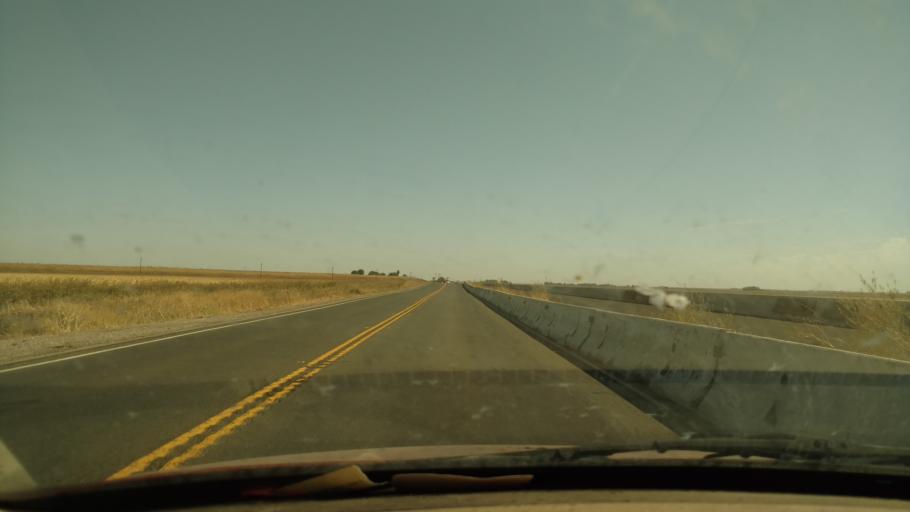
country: US
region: California
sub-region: Contra Costa County
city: Bethel Island
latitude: 38.1203
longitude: -121.5671
